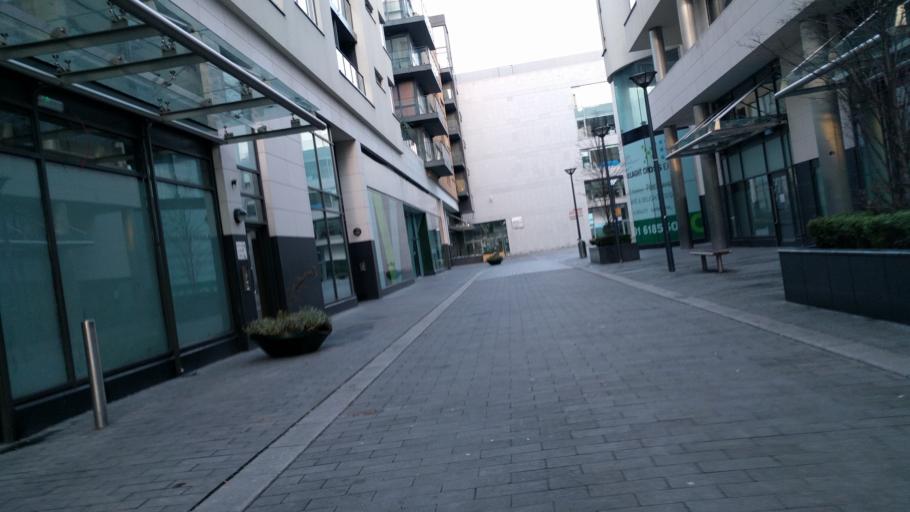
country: IE
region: Leinster
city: Tallaght
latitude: 53.2882
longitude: -6.3752
